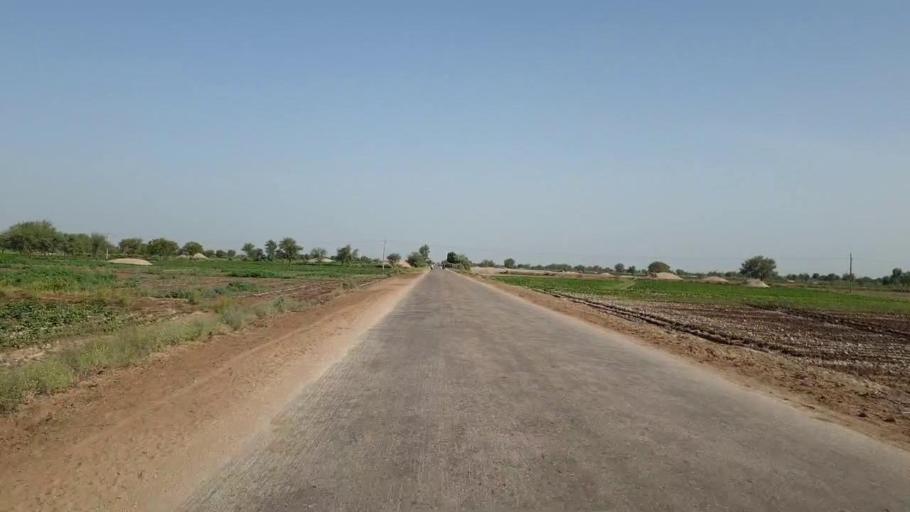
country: PK
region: Sindh
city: Nawabshah
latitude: 26.1369
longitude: 68.4535
